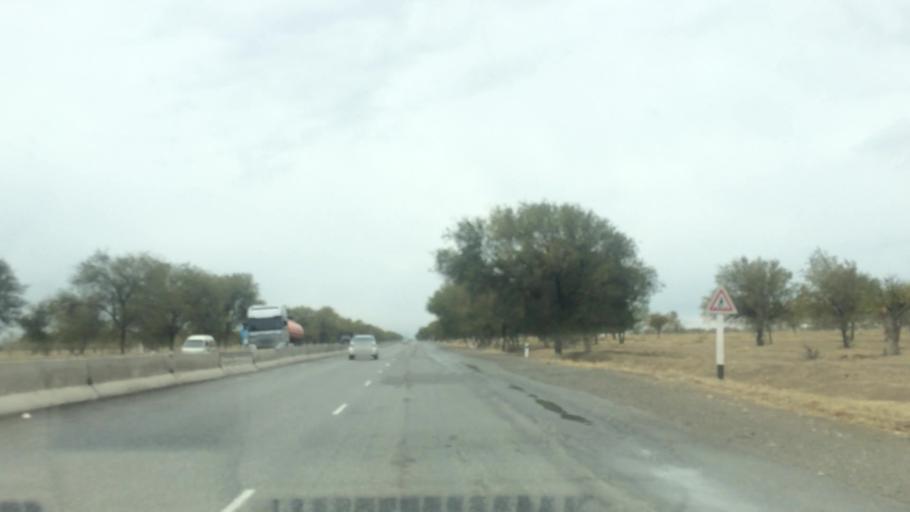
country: UZ
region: Samarqand
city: Bulung'ur
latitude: 39.8107
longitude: 67.3663
